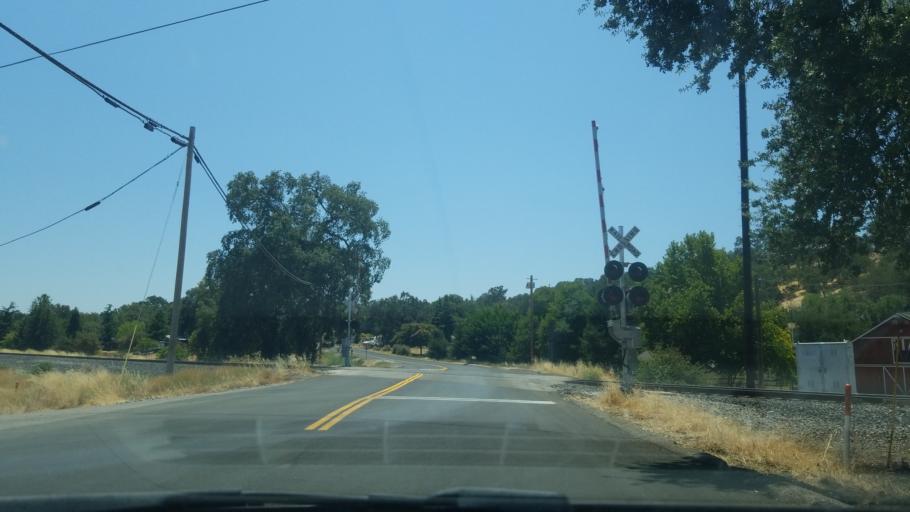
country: US
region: California
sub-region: San Luis Obispo County
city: Atascadero
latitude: 35.4896
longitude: -120.6475
